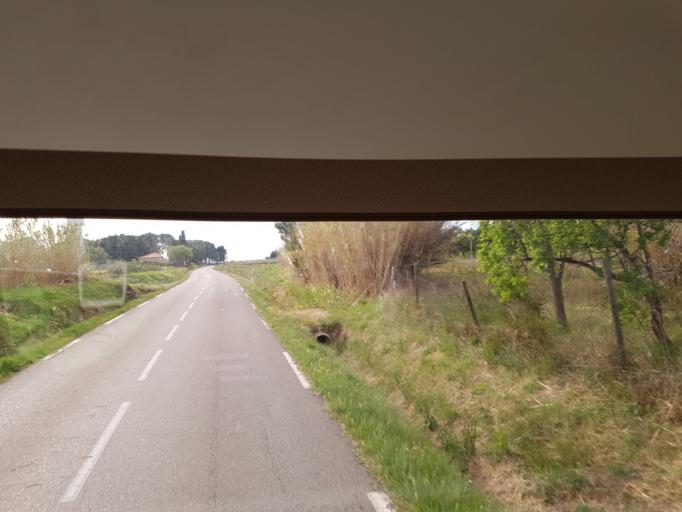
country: FR
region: Languedoc-Roussillon
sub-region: Departement de l'Herault
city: Pomerols
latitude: 43.3685
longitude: 3.5043
